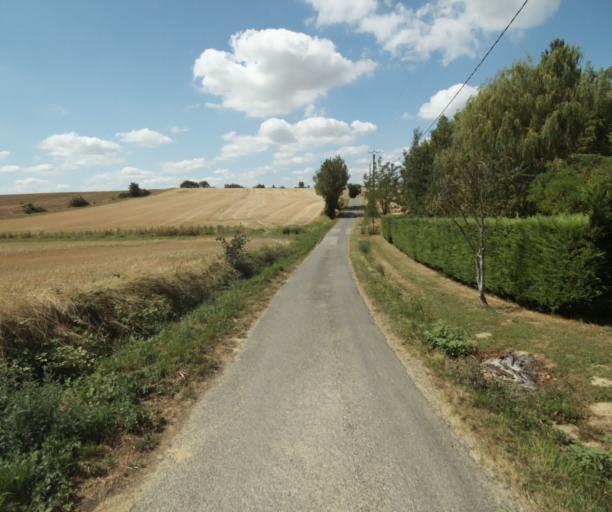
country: FR
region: Midi-Pyrenees
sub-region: Departement de la Haute-Garonne
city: Auriac-sur-Vendinelle
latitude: 43.4786
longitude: 1.8266
